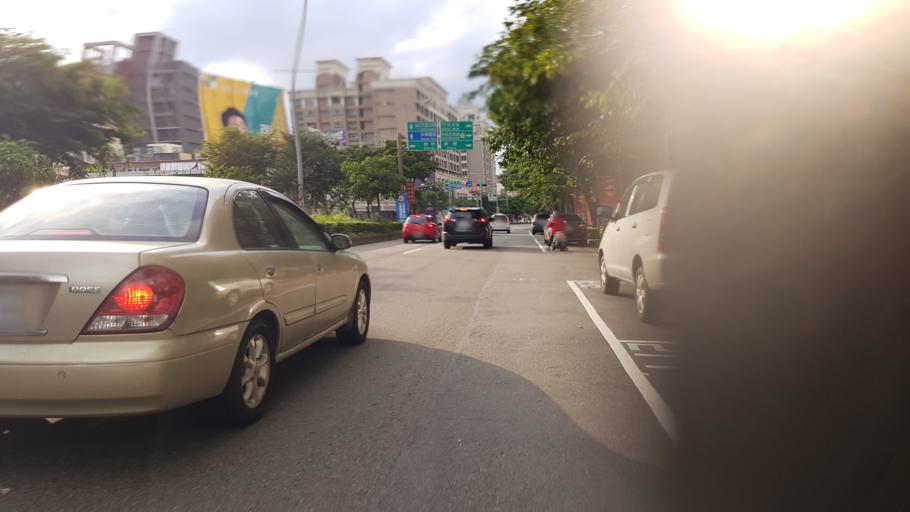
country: TW
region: Taiwan
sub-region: Hsinchu
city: Zhubei
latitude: 24.8081
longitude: 121.0340
